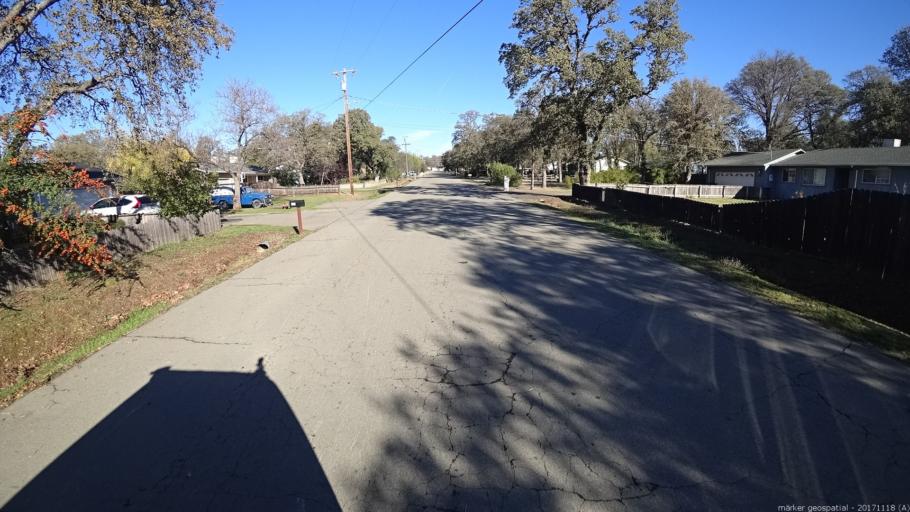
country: US
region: California
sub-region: Shasta County
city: Cottonwood
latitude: 40.3895
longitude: -122.3197
